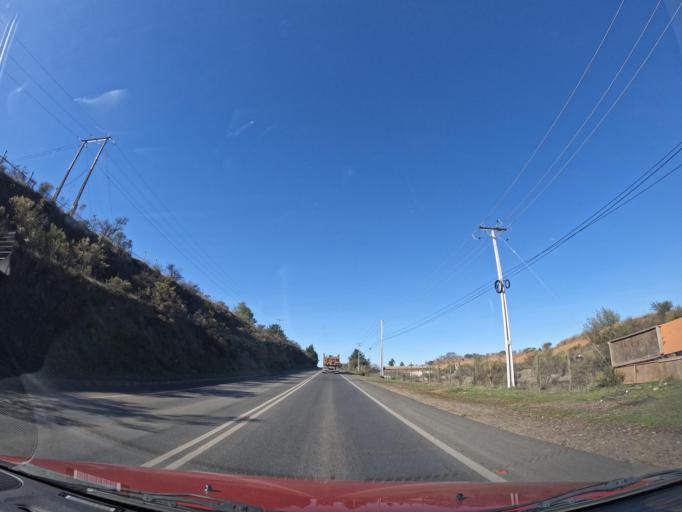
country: CL
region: Maule
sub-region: Provincia de Cauquenes
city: Cauquenes
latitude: -35.9607
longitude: -72.2567
